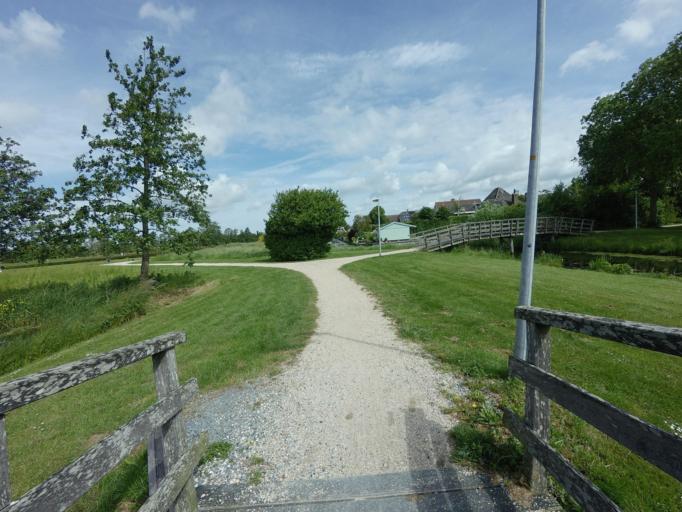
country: NL
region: North Holland
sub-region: Gemeente Hoorn
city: Hoorn
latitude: 52.6791
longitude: 5.0170
